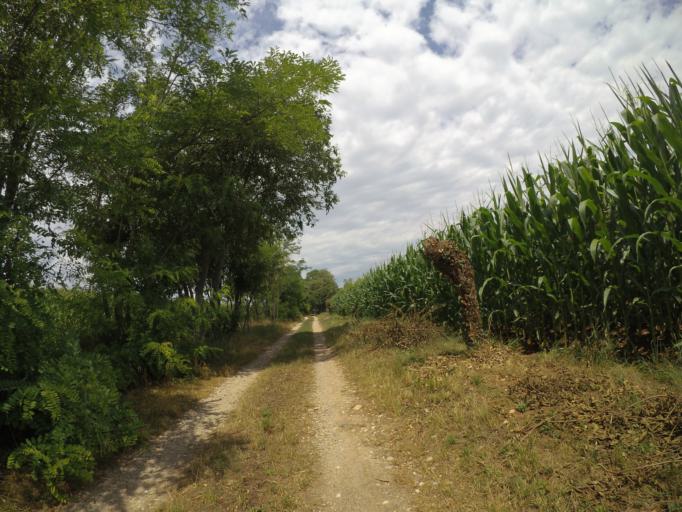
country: IT
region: Friuli Venezia Giulia
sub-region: Provincia di Udine
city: Bertiolo
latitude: 45.9629
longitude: 13.0649
